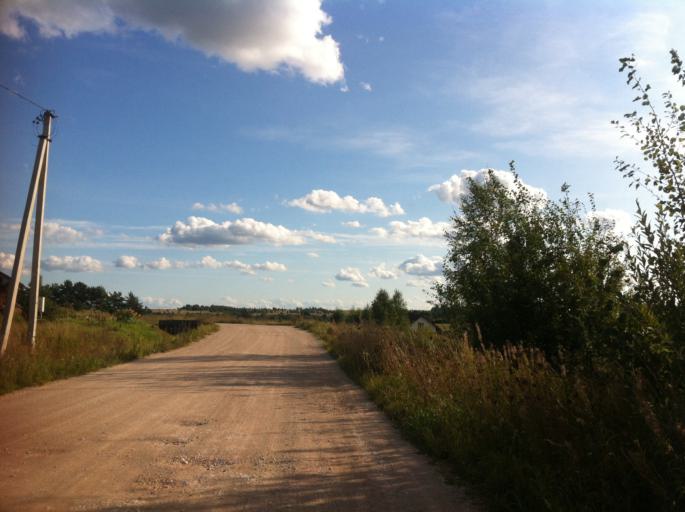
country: RU
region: Pskov
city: Izborsk
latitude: 57.8250
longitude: 27.9656
